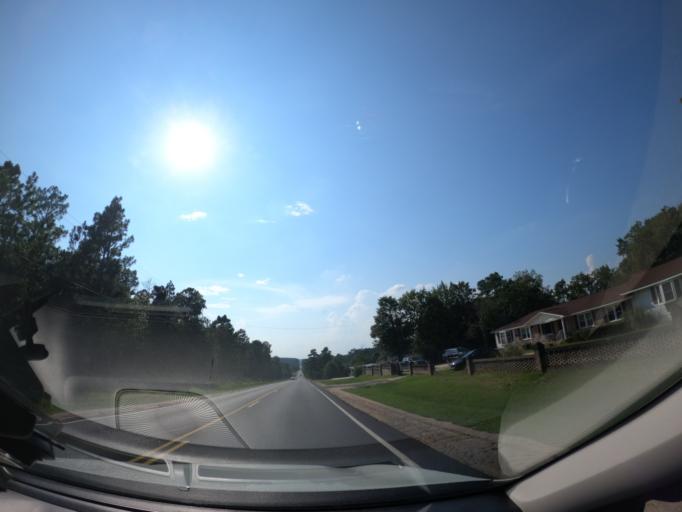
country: US
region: South Carolina
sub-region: Aiken County
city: New Ellenton
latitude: 33.3953
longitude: -81.7419
